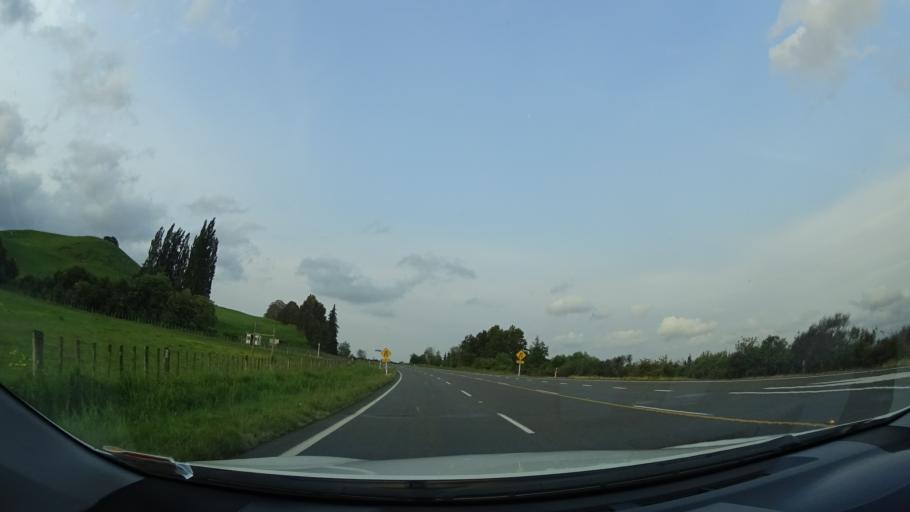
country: NZ
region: Manawatu-Wanganui
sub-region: Ruapehu District
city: Waiouru
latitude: -39.7515
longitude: 175.8340
